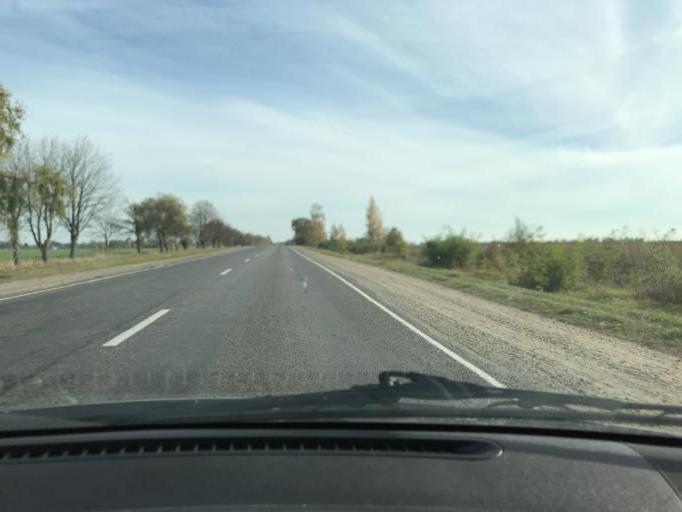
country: BY
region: Brest
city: Asnyezhytsy
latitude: 52.2062
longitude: 26.0545
